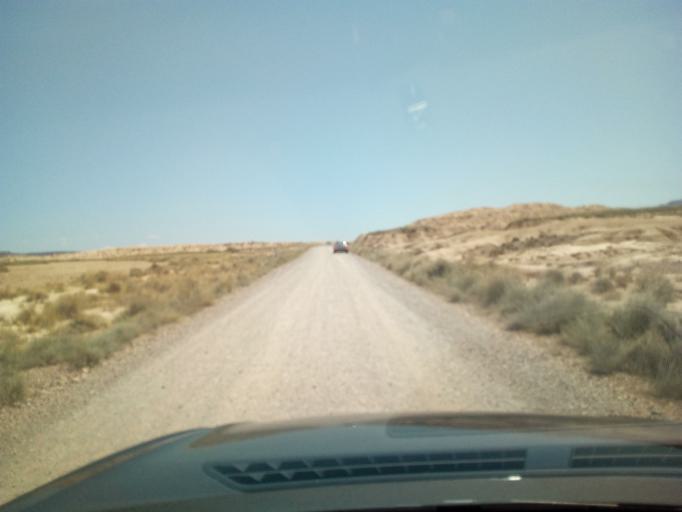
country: ES
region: Navarre
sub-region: Provincia de Navarra
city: Arguedas
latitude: 42.1824
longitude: -1.4721
